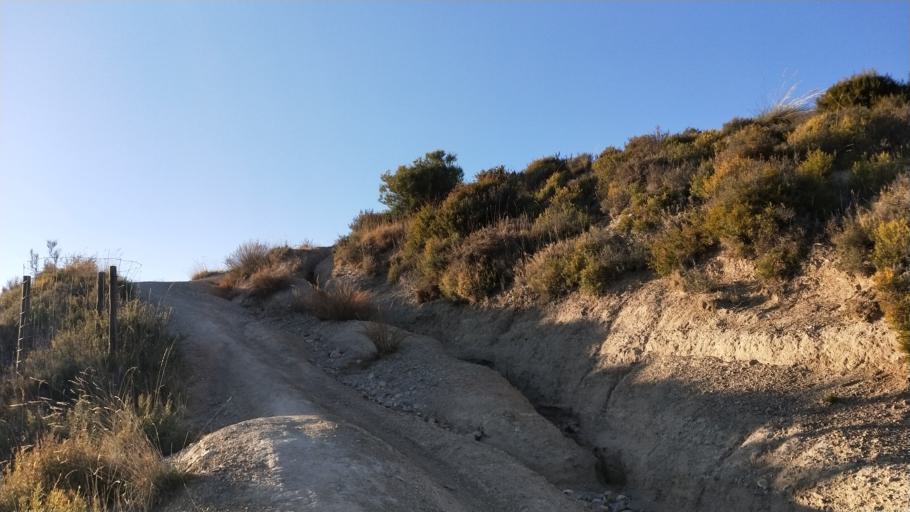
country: ES
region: Andalusia
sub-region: Provincia de Granada
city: Dudar
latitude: 37.1965
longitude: -3.5019
